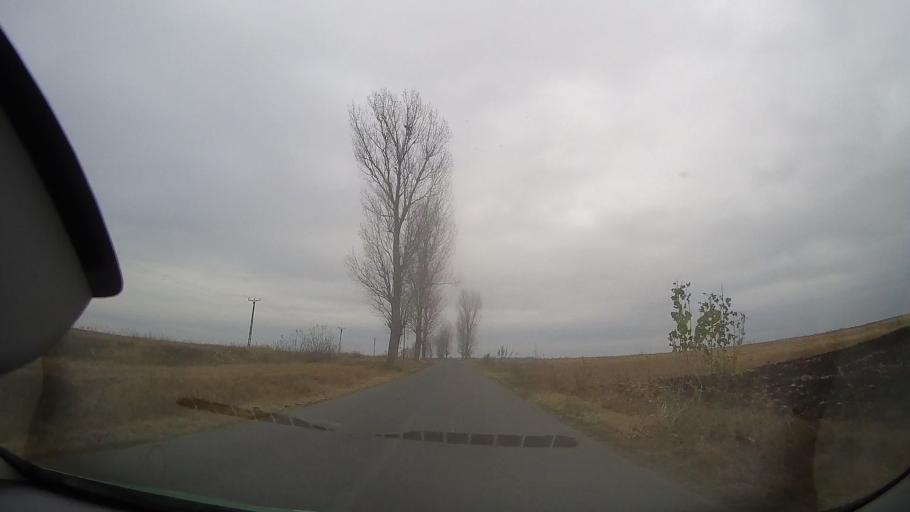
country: RO
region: Braila
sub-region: Comuna Rosiori
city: Rosiori
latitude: 44.8173
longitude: 27.3618
